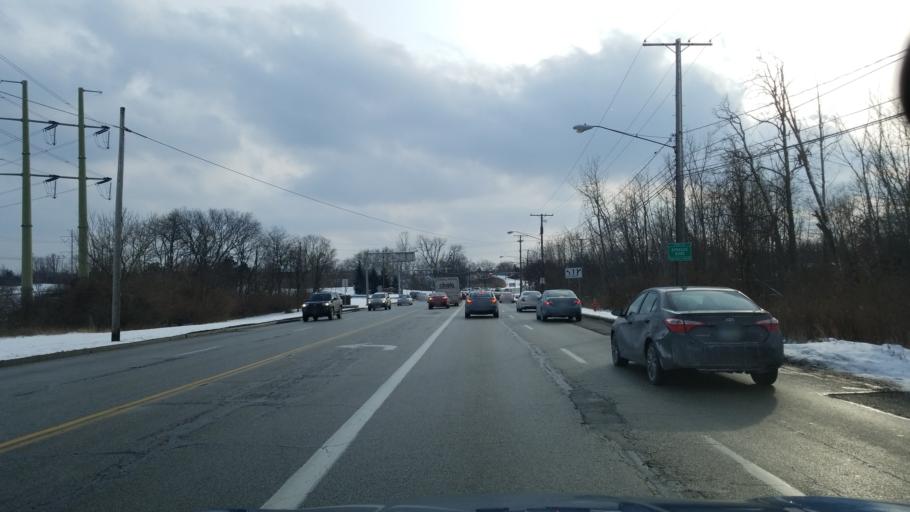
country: US
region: Ohio
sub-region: Cuyahoga County
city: Middleburg Heights
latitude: 41.3522
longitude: -81.8206
